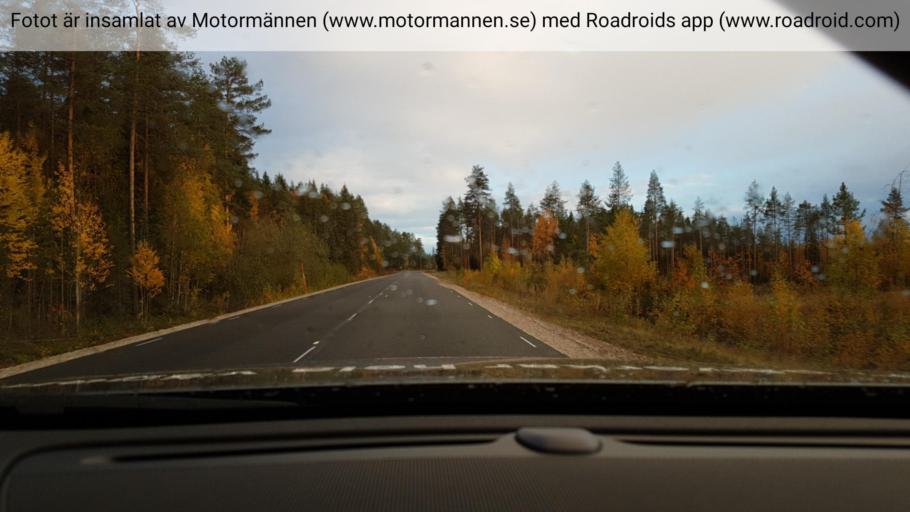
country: SE
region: Norrbotten
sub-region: Overkalix Kommun
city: OEverkalix
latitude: 66.3988
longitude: 22.8134
